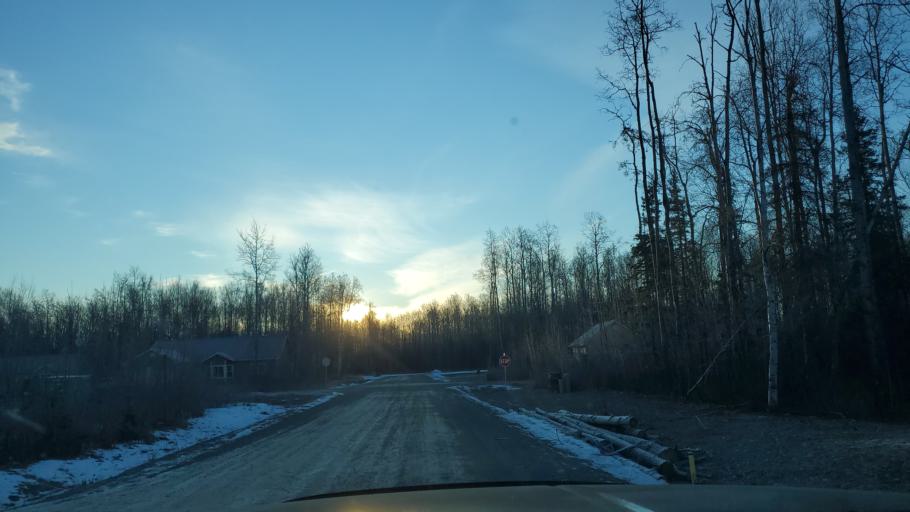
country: US
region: Alaska
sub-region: Matanuska-Susitna Borough
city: Lakes
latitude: 61.6564
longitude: -149.3404
